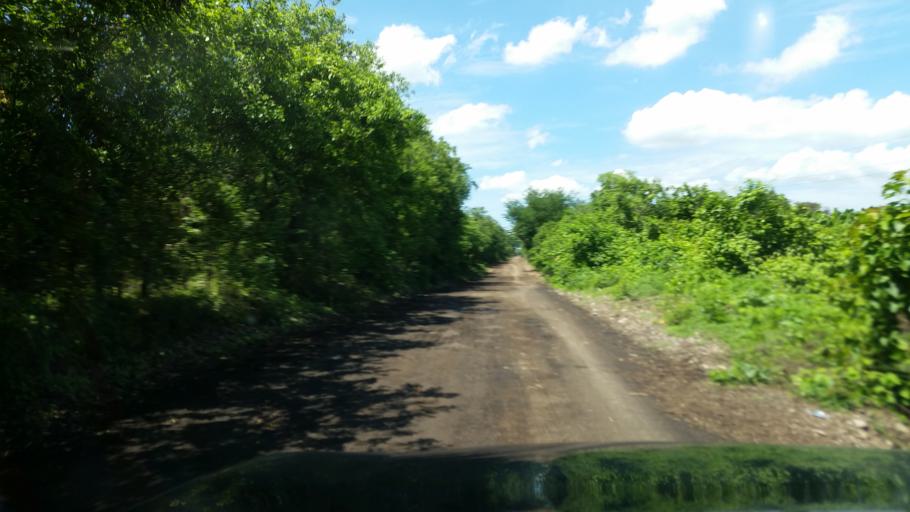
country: NI
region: Chinandega
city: Puerto Morazan
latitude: 12.7607
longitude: -87.1334
